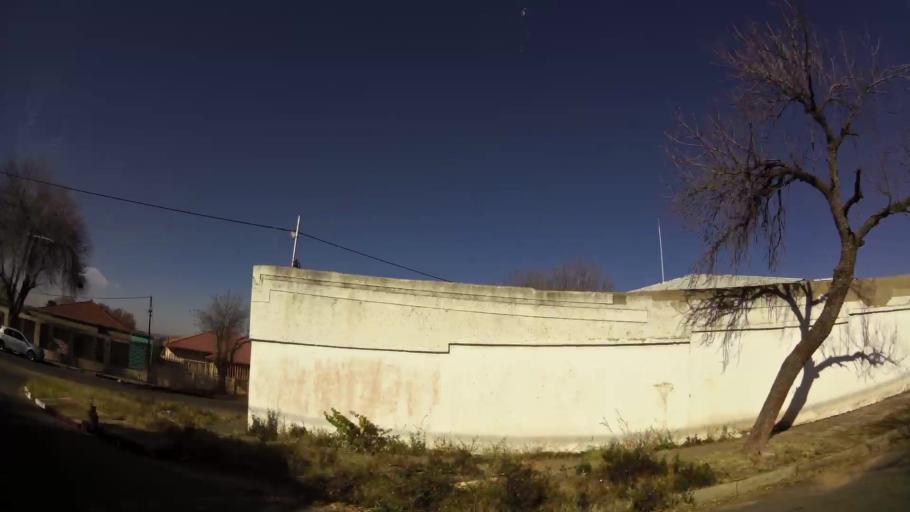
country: ZA
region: Gauteng
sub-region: City of Johannesburg Metropolitan Municipality
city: Johannesburg
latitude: -26.1966
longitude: 28.0016
